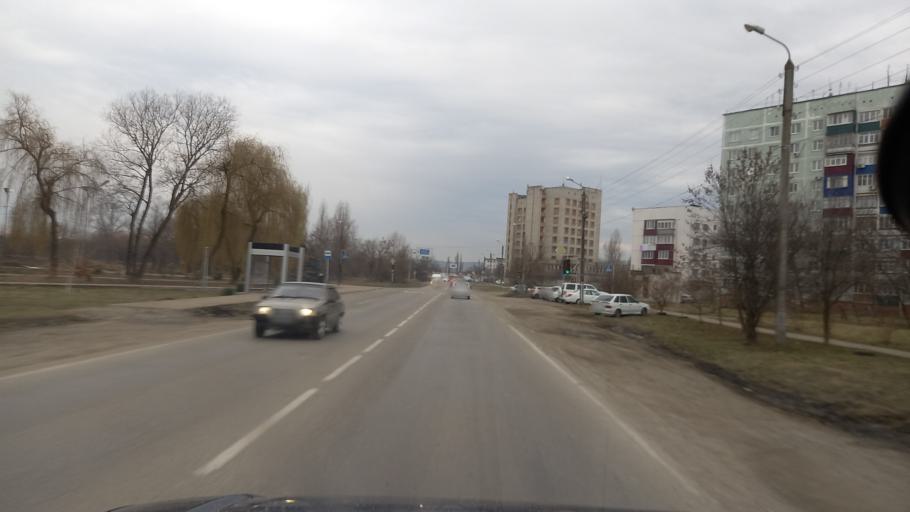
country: RU
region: Adygeya
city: Maykop
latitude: 44.5774
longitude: 40.1350
